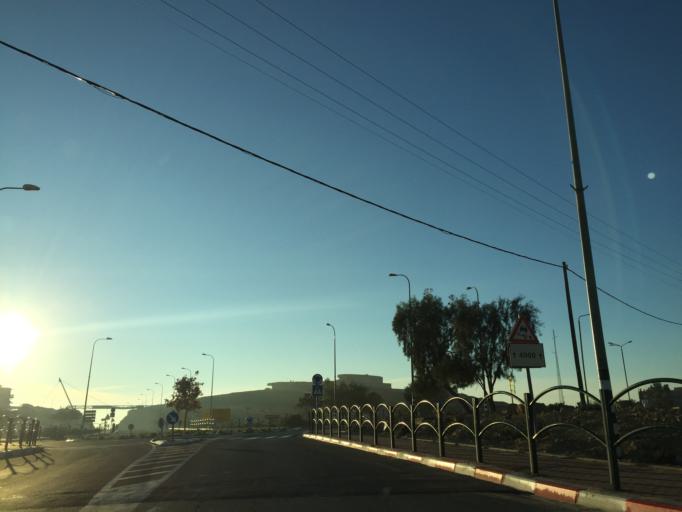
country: IL
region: Southern District
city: Mitzpe Ramon
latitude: 30.6115
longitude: 34.8046
